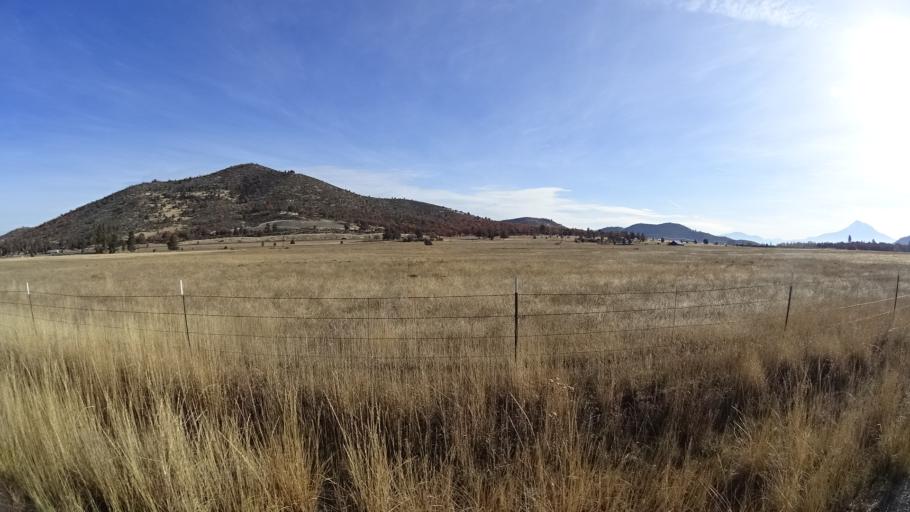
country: US
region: California
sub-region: Siskiyou County
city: Yreka
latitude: 41.6764
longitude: -122.6329
